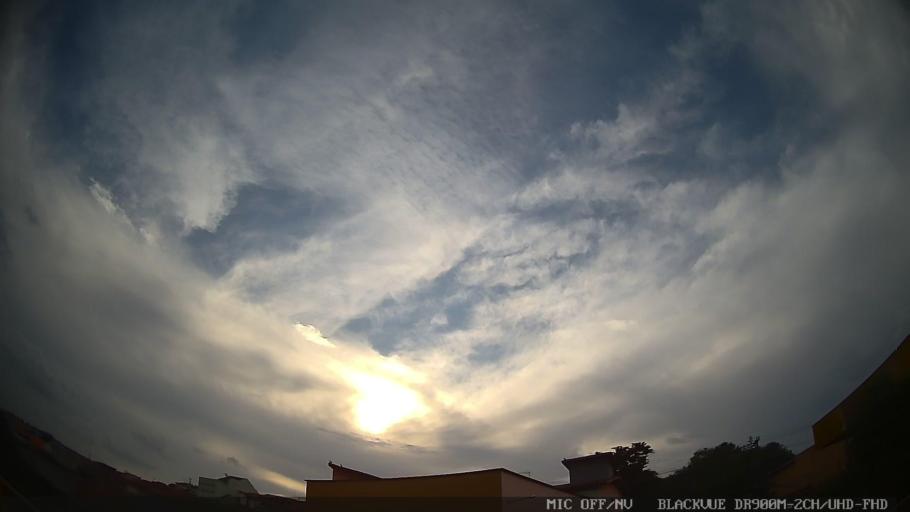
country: BR
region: Sao Paulo
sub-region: Braganca Paulista
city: Braganca Paulista
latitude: -22.9451
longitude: -46.5413
